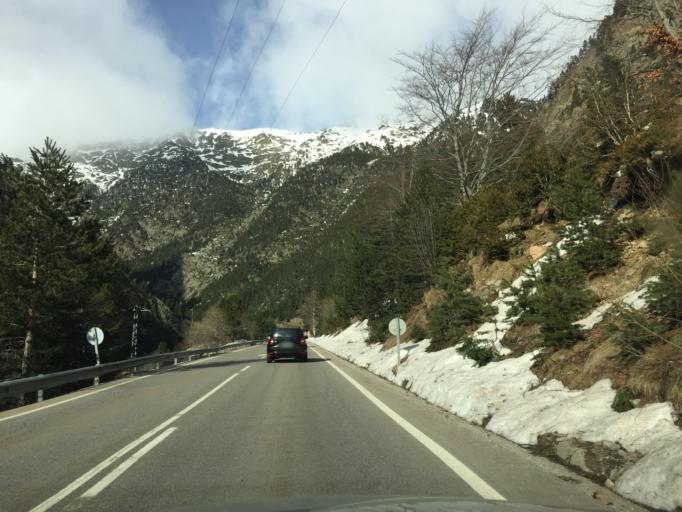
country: ES
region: Aragon
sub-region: Provincia de Huesca
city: Bielsa
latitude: 42.7084
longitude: 0.2023
